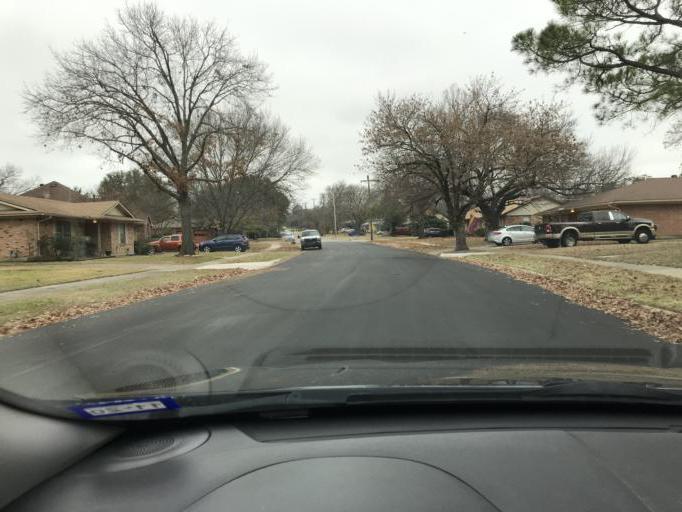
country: US
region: Texas
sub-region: Denton County
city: Denton
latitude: 33.2261
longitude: -97.1567
